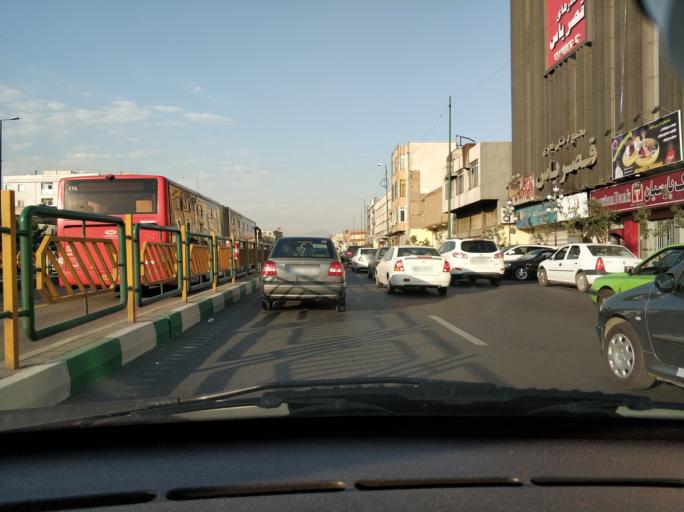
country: IR
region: Tehran
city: Tehran
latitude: 35.7085
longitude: 51.4703
